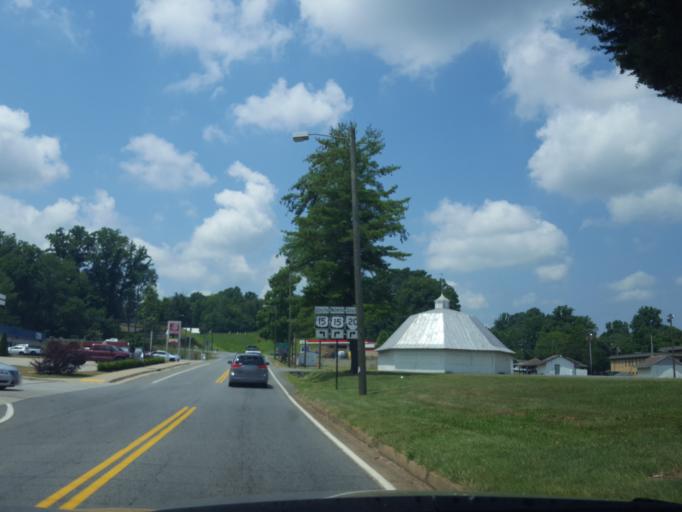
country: US
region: Virginia
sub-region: Orange County
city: Orange
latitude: 38.2402
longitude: -78.1103
